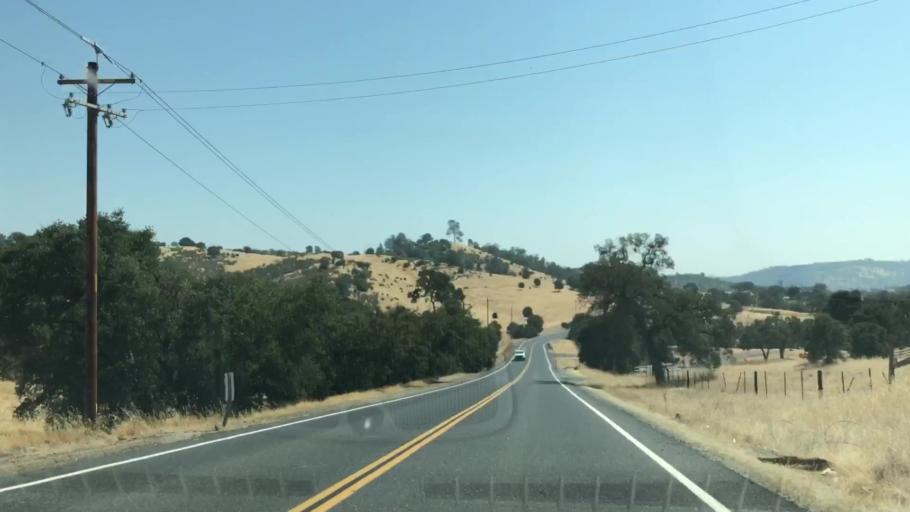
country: US
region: California
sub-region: Calaveras County
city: Copperopolis
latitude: 37.9295
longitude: -120.5992
